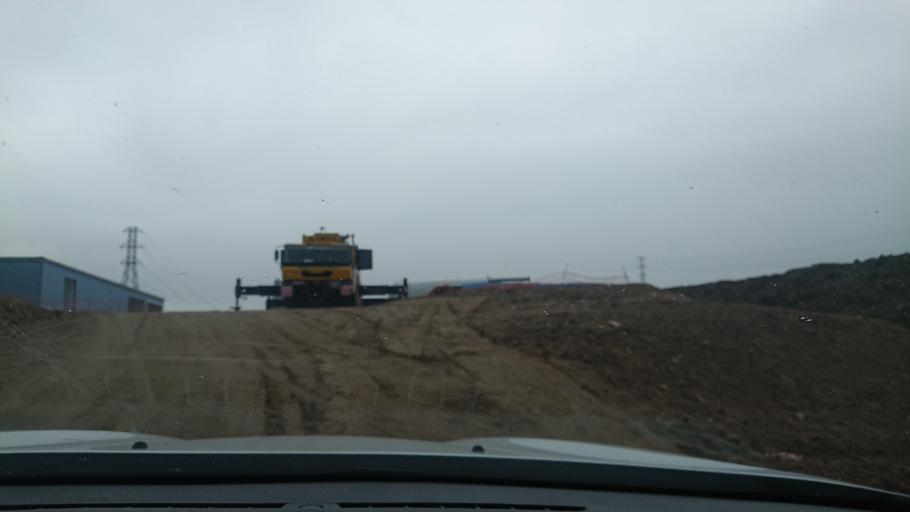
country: TR
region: Aksaray
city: Agacoren
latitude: 38.9455
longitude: 33.9146
